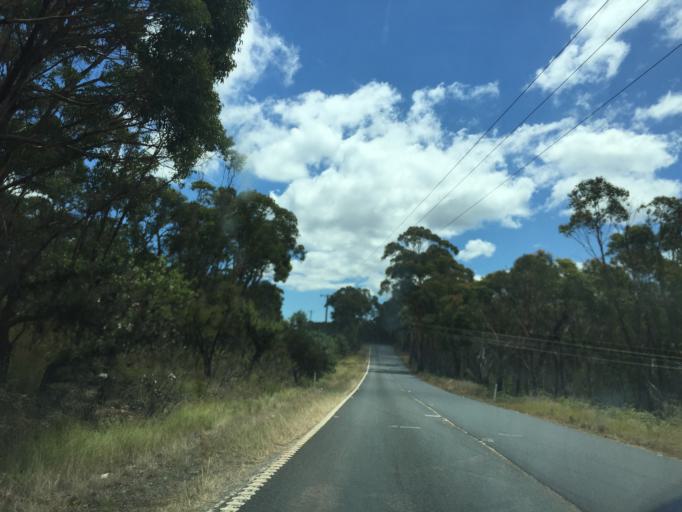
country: AU
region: New South Wales
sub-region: Blue Mountains Municipality
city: Blackheath
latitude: -33.5377
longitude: 150.3273
